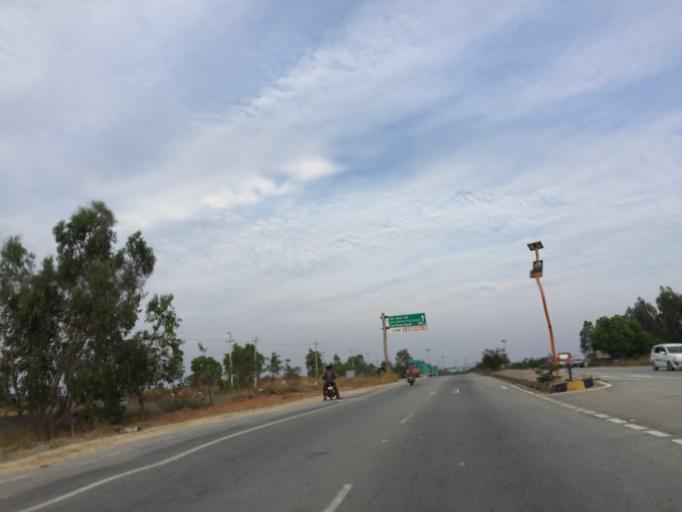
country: IN
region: Karnataka
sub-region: Kolar
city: Mulbagal
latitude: 13.1470
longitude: 78.2850
